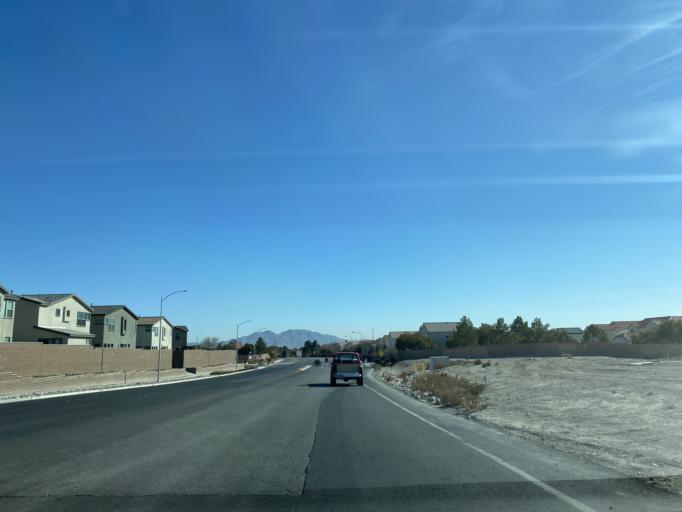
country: US
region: Nevada
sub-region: Clark County
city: North Las Vegas
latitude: 36.2846
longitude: -115.1512
